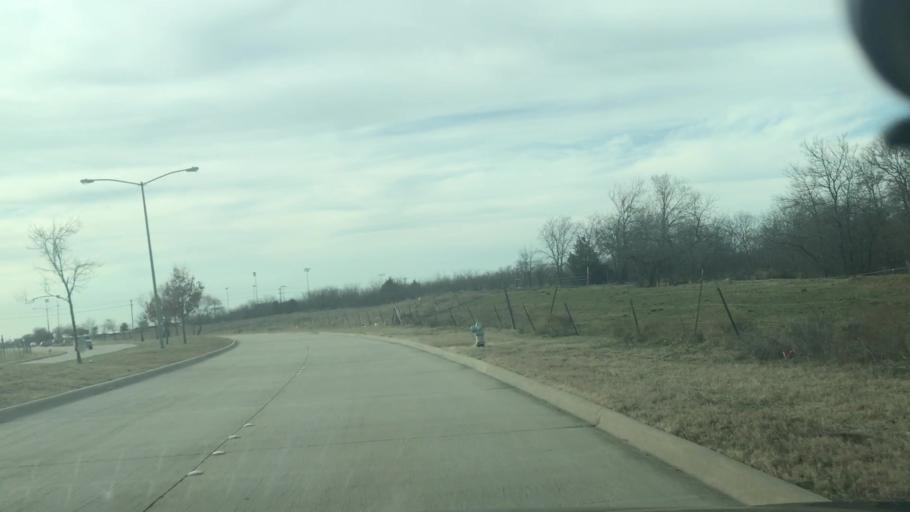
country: US
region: Texas
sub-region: Dallas County
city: Coppell
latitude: 32.9998
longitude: -97.0245
